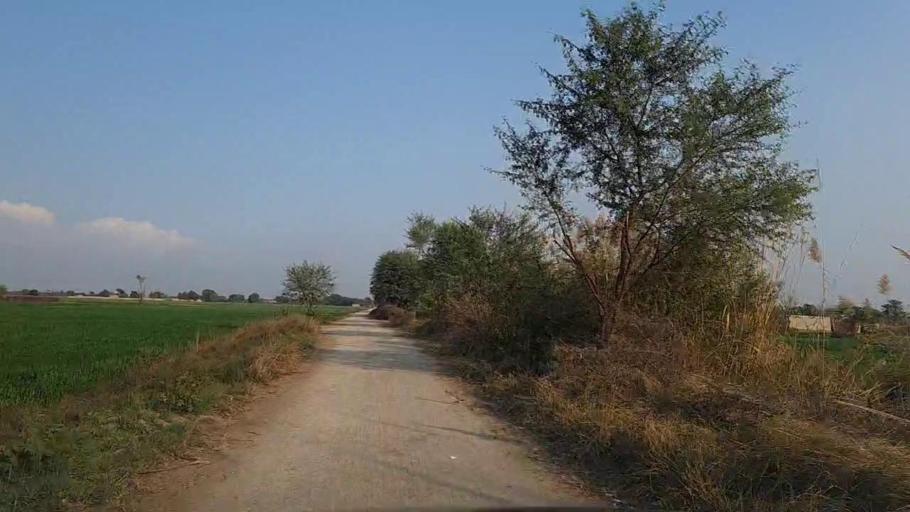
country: PK
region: Sindh
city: Jam Sahib
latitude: 26.3438
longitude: 68.5823
